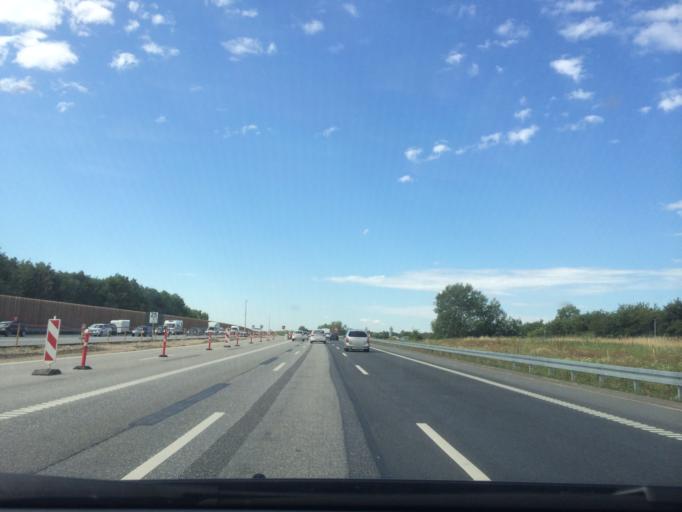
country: DK
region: Zealand
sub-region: Solrod Kommune
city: Solrod Strand
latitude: 55.5718
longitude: 12.2430
